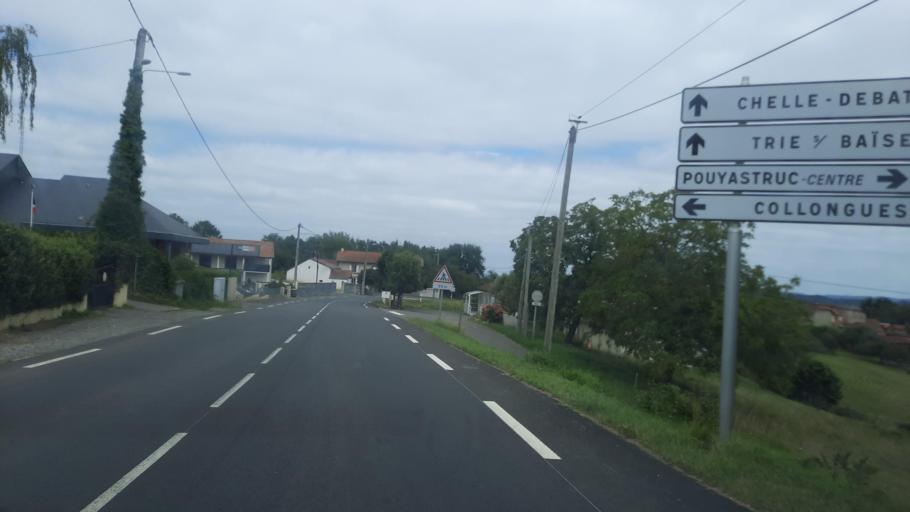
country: FR
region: Midi-Pyrenees
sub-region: Departement des Hautes-Pyrenees
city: Orleix
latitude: 43.2662
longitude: 0.1573
